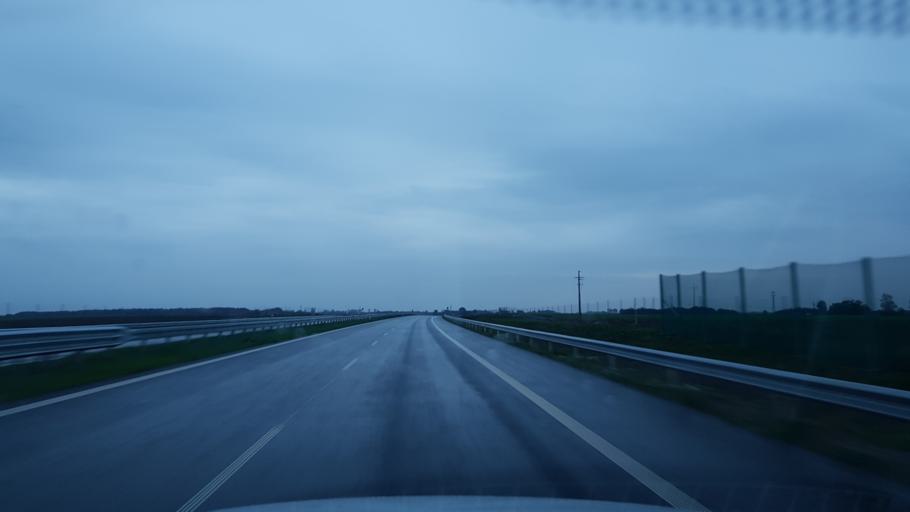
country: PL
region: West Pomeranian Voivodeship
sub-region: Powiat gryficki
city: Brojce
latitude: 53.9961
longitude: 15.4477
